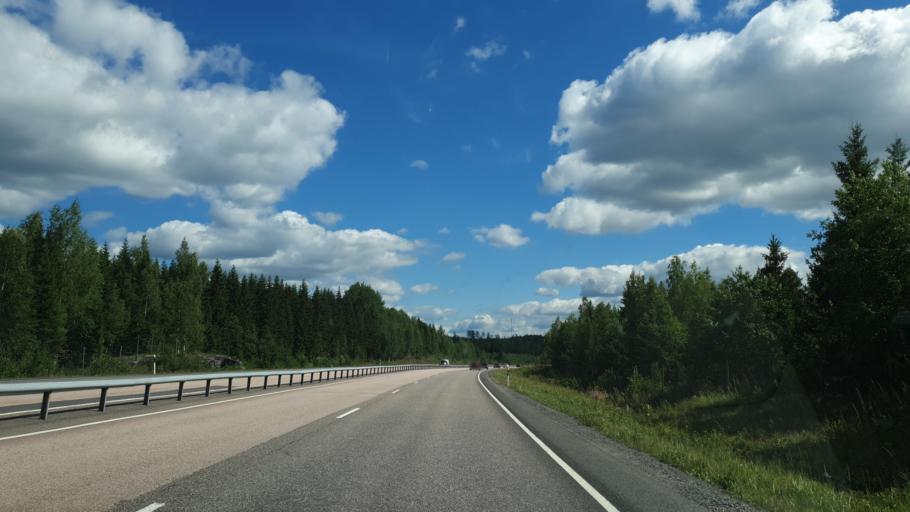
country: FI
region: Pirkanmaa
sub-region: Tampere
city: Orivesi
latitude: 61.7103
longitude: 24.5284
